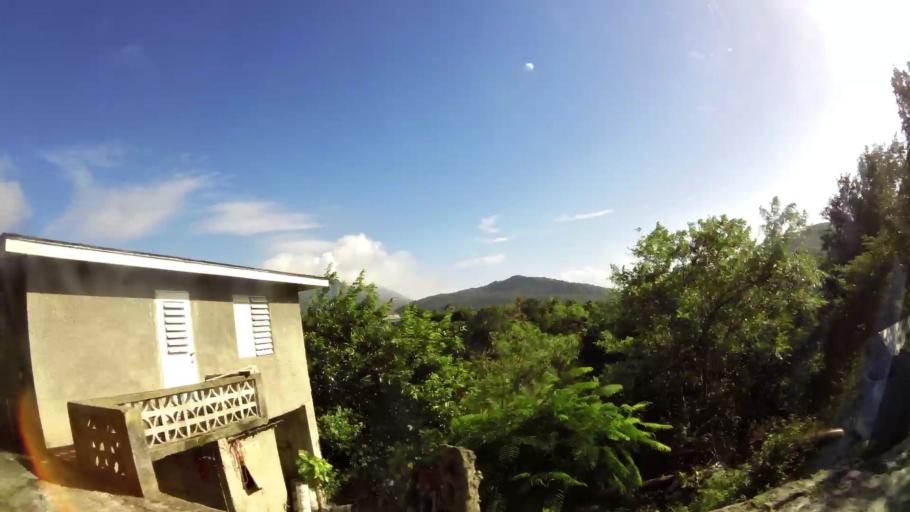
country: MS
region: Saint Peter
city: Saint Peters
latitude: 16.7488
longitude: -62.2191
